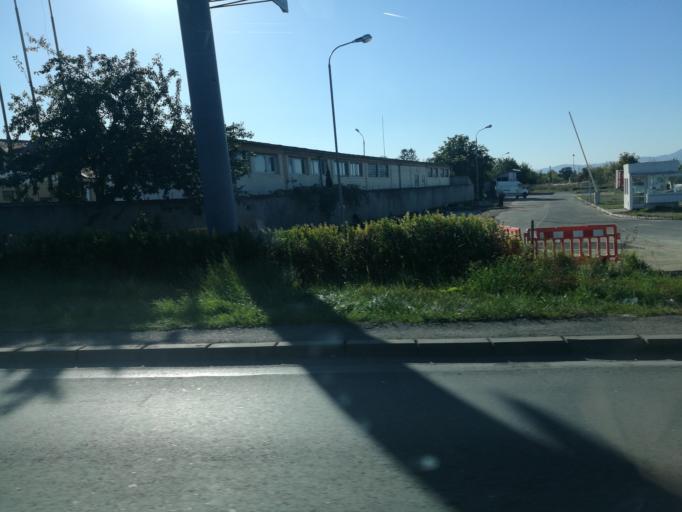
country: RO
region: Brasov
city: Brasov
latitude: 45.6712
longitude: 25.5903
